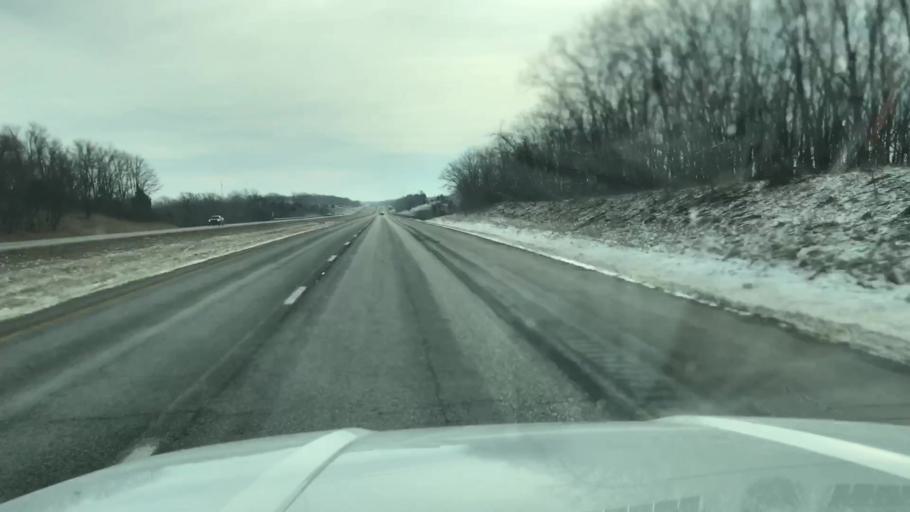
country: US
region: Missouri
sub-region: Holt County
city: Oregon
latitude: 39.9896
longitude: -95.0435
